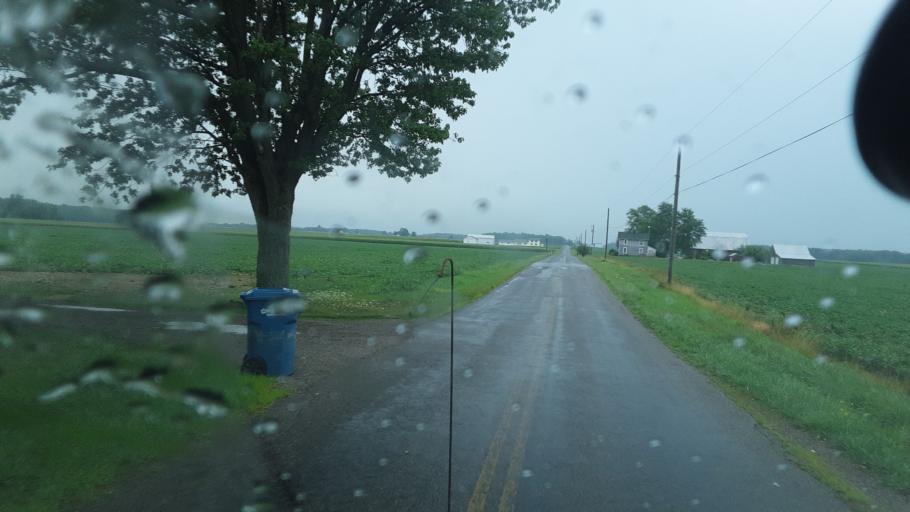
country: US
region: Ohio
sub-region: Williams County
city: Edgerton
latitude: 41.5196
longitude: -84.7883
